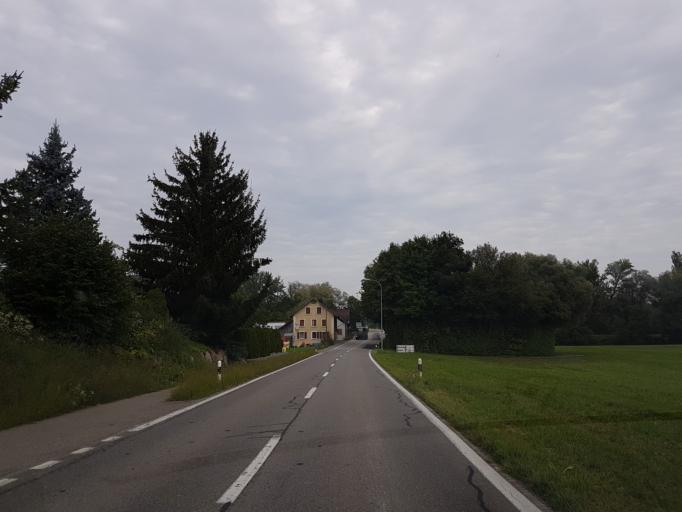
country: CH
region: Zurich
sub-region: Bezirk Affoltern
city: Obfelden / Oberlunnern
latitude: 47.2641
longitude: 8.3977
